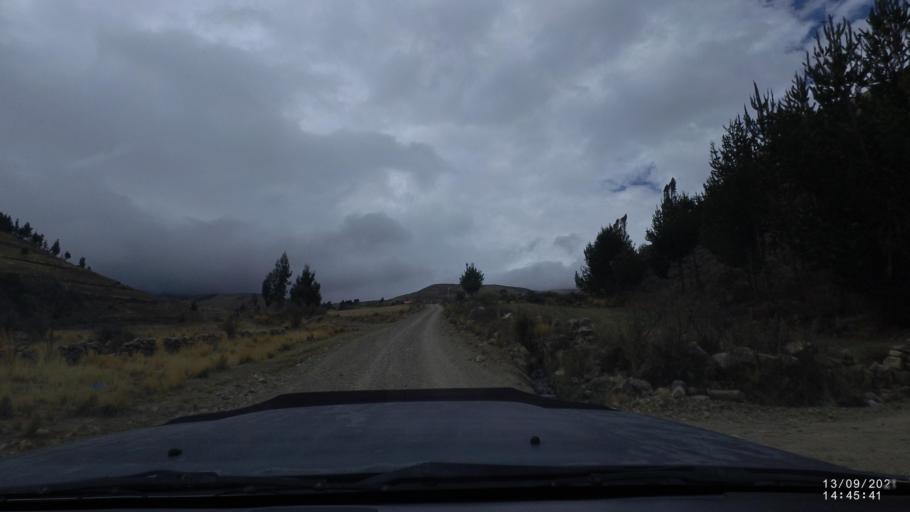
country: BO
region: Cochabamba
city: Colomi
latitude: -17.3525
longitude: -65.8078
